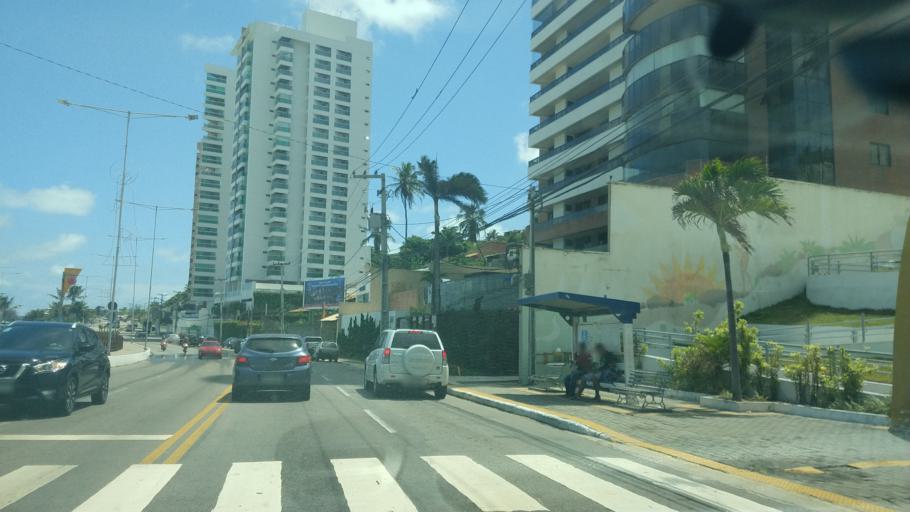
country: BR
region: Rio Grande do Norte
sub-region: Natal
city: Natal
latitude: -5.7904
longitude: -35.1881
